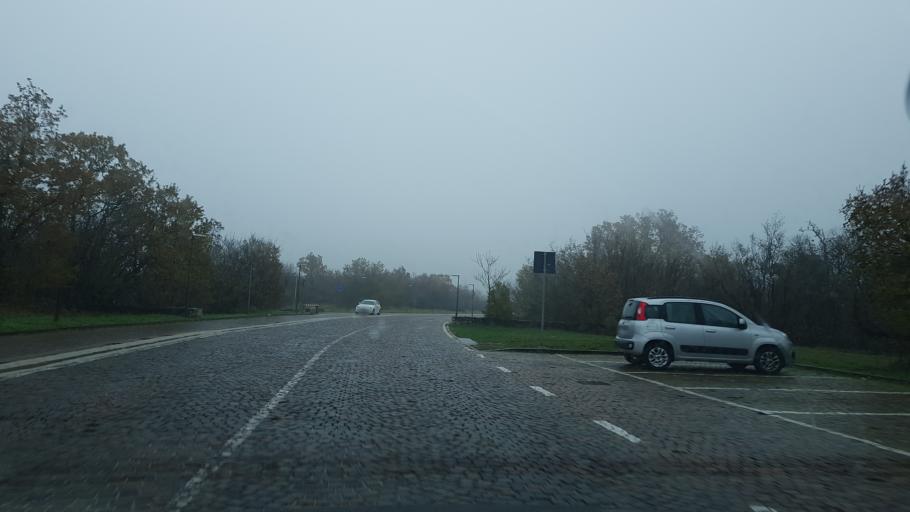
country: IT
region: Friuli Venezia Giulia
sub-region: Provincia di Trieste
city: Domio
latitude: 45.6432
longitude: 13.8489
